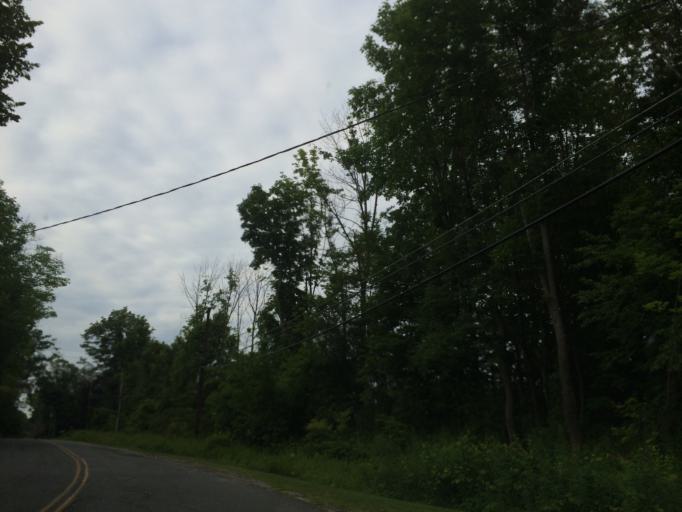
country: US
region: Massachusetts
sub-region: Berkshire County
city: Lanesborough
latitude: 42.5373
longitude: -73.2290
